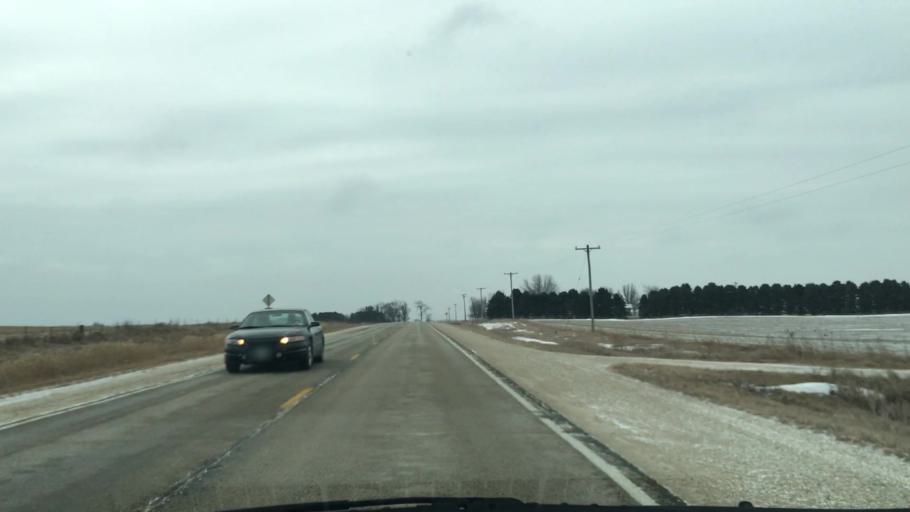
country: US
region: Iowa
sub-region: Fayette County
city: West Union
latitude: 43.0266
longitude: -91.8295
